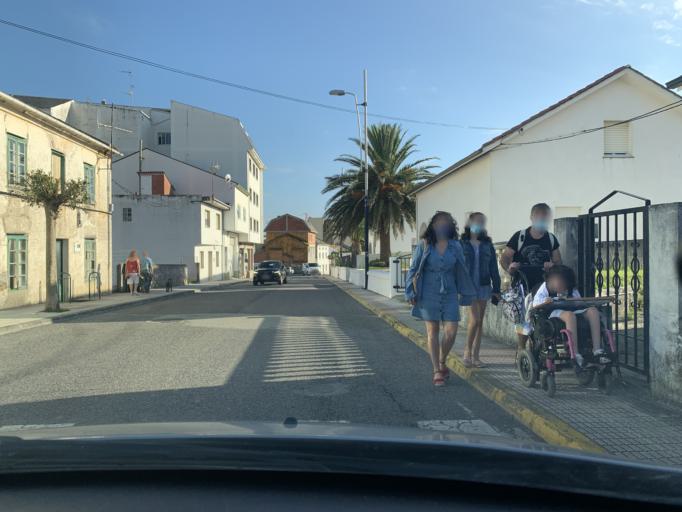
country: ES
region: Galicia
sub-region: Provincia de Lugo
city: Foz
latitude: 43.5703
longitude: -7.2531
